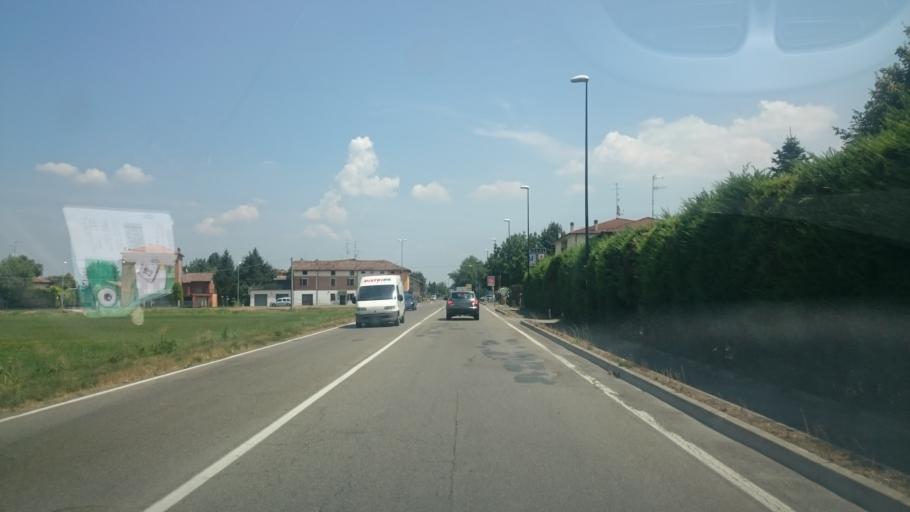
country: IT
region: Emilia-Romagna
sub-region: Provincia di Reggio Emilia
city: Bagno
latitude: 44.6568
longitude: 10.7522
